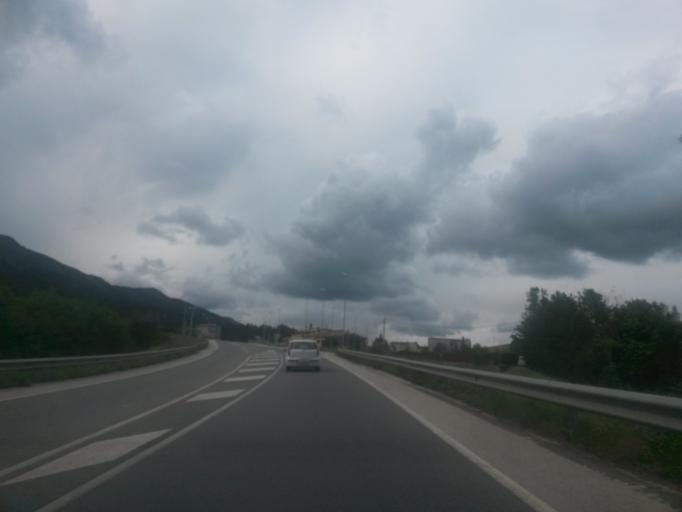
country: ES
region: Catalonia
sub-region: Provincia de Girona
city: Brunyola
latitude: 41.9180
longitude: 2.6551
